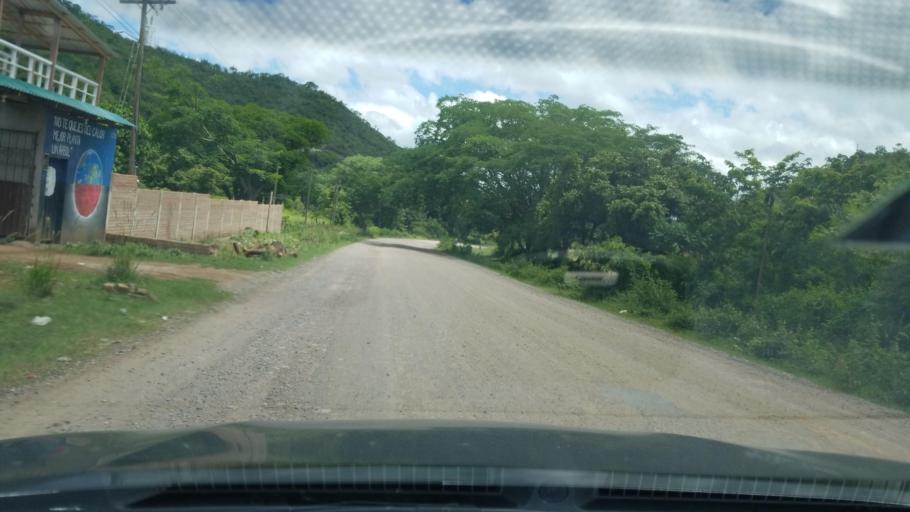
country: HN
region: Francisco Morazan
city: Talanga
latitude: 14.3881
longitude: -87.0741
